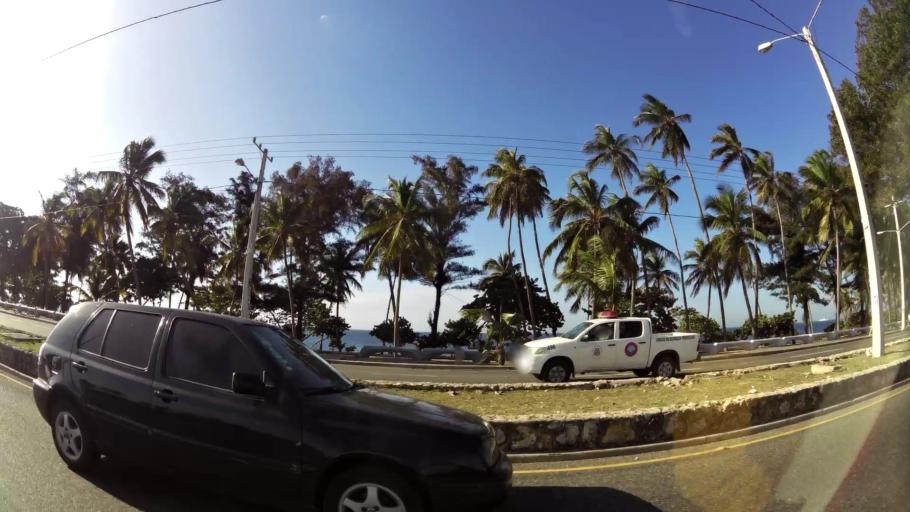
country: DO
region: Santo Domingo
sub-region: Santo Domingo
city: Santo Domingo Este
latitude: 18.4693
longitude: -69.8567
